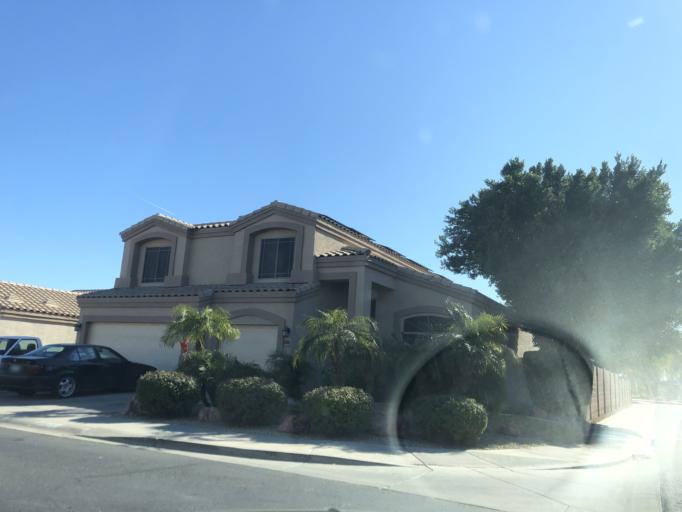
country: US
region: Arizona
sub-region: Maricopa County
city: El Mirage
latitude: 33.6146
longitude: -112.3411
